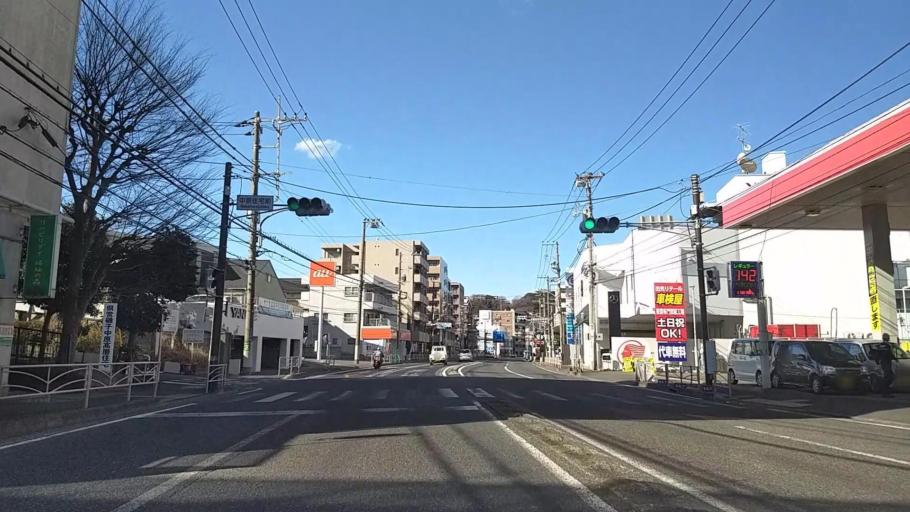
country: JP
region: Kanagawa
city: Yokohama
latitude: 35.3904
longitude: 139.6154
